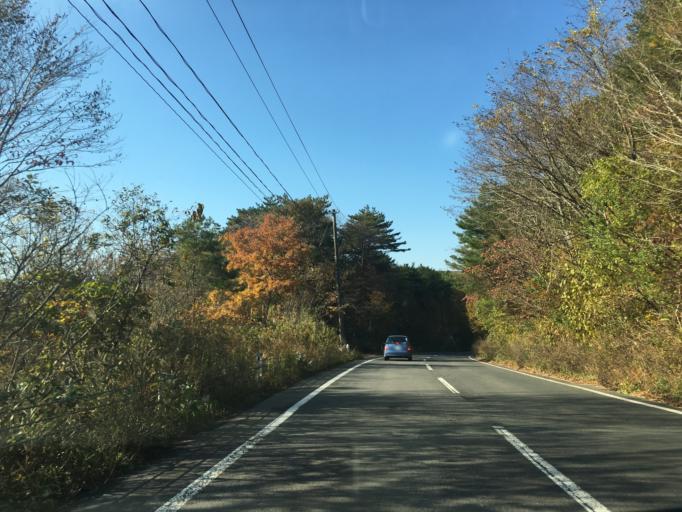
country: JP
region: Fukushima
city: Sukagawa
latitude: 37.2633
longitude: 140.1006
